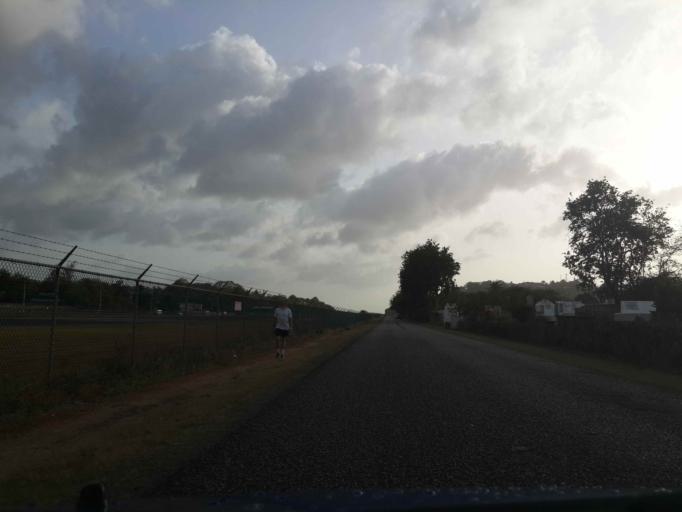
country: LC
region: Castries Quarter
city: Bisee
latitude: 14.0222
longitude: -60.9866
